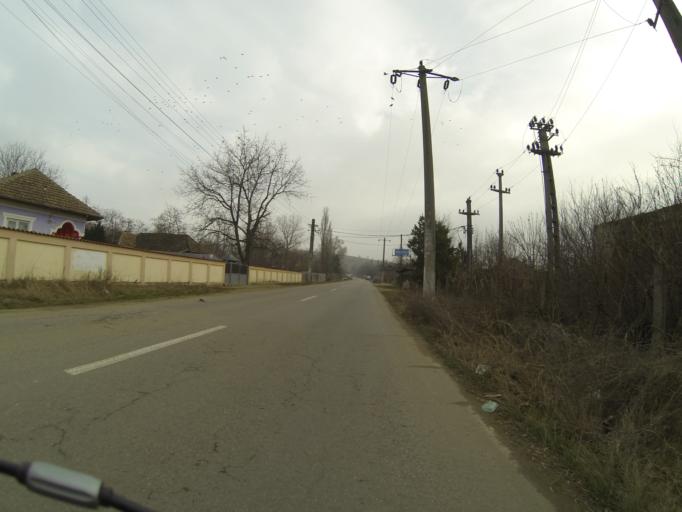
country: RO
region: Mehedinti
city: Vanju-Mare
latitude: 44.4197
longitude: 22.8744
